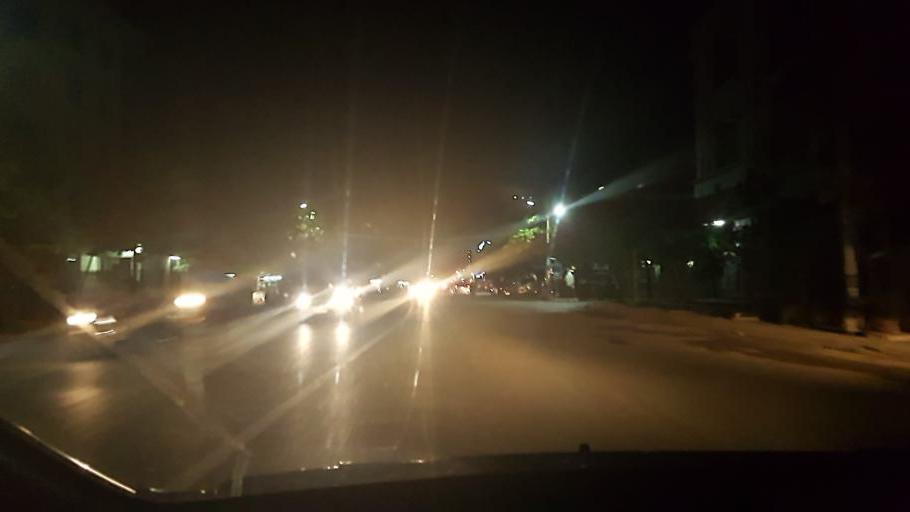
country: MM
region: Mandalay
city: Mandalay
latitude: 21.9744
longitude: 96.0955
